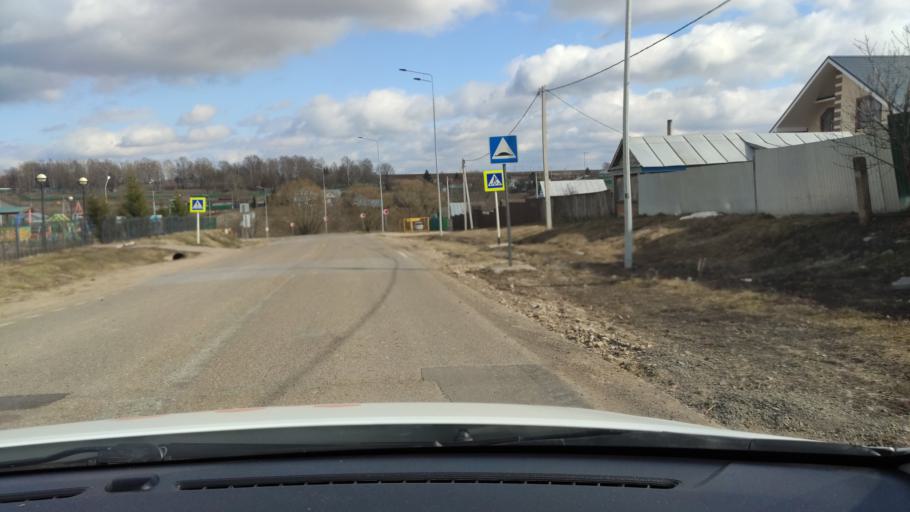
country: RU
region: Tatarstan
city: Vysokaya Gora
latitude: 56.2201
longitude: 49.2722
